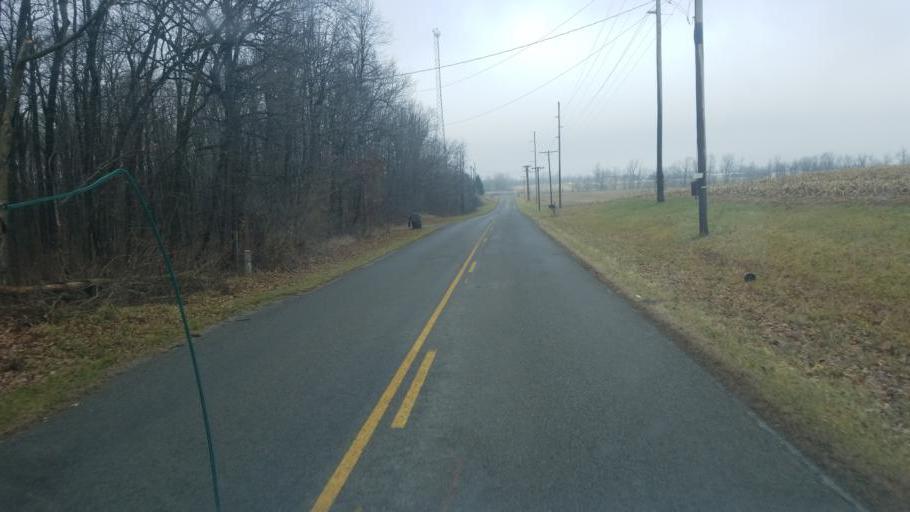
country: US
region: Ohio
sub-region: Champaign County
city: North Lewisburg
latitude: 40.3149
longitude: -83.5847
